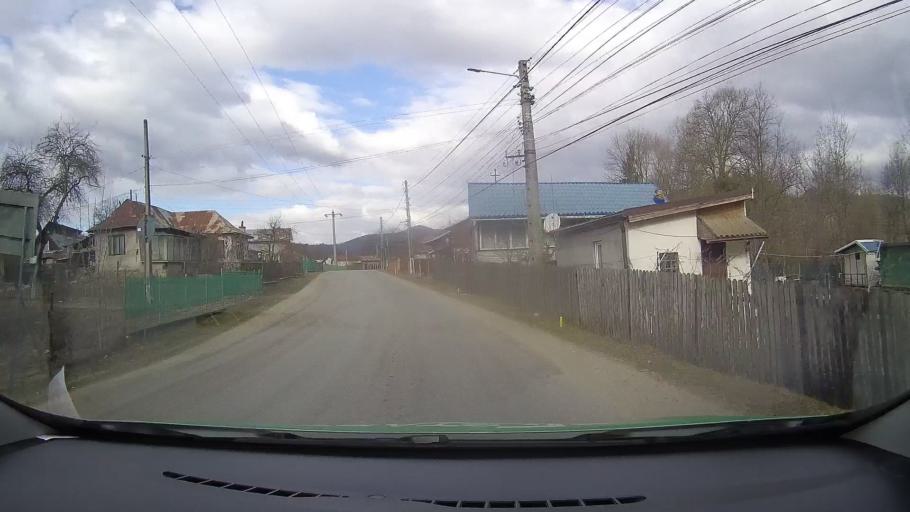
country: RO
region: Prahova
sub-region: Comuna Provita de Jos
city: Provita de Jos
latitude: 45.1287
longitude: 25.6504
